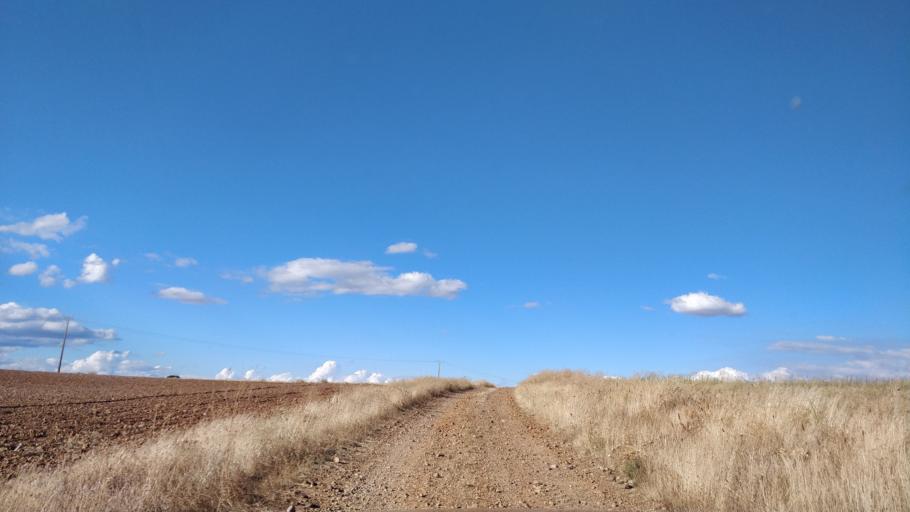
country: ES
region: Castille and Leon
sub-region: Provincia de Leon
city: Santa Cristina de Valmadrigal
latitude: 42.3383
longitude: -5.2743
